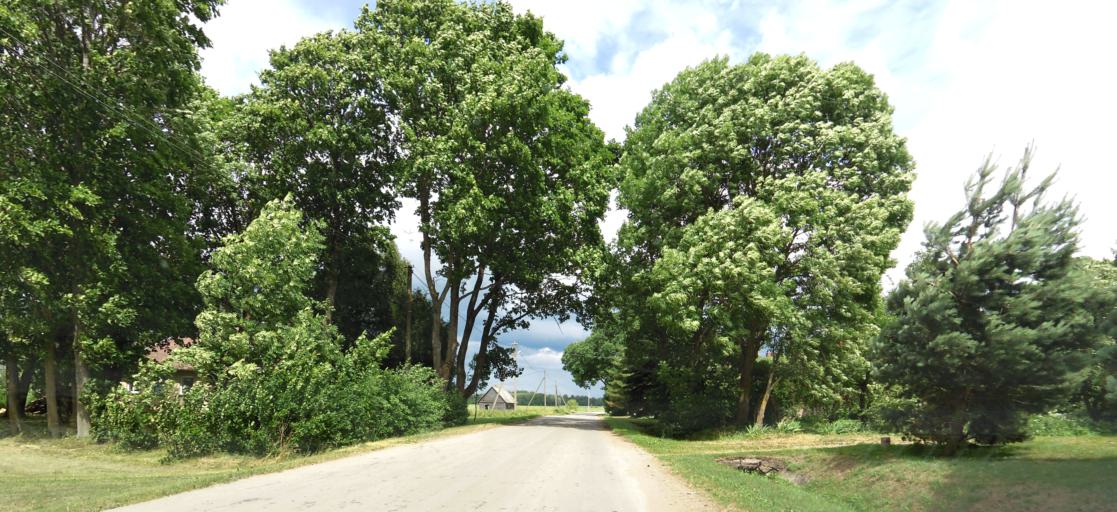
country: LT
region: Panevezys
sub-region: Birzai
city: Birzai
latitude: 56.2967
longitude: 24.7432
